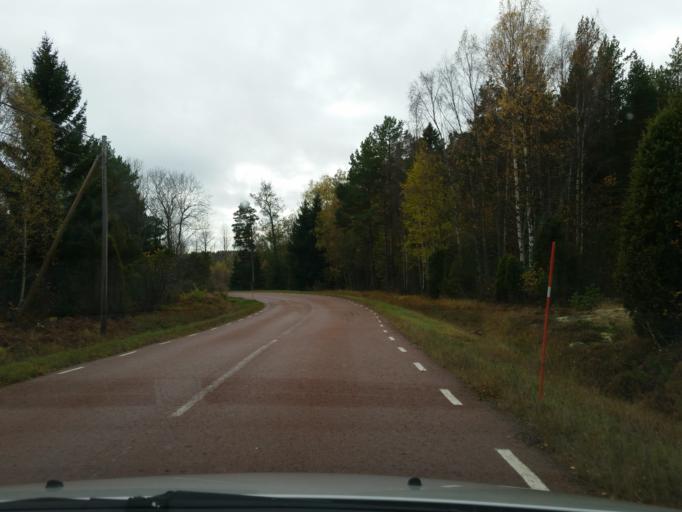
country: AX
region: Alands landsbygd
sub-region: Lemland
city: Lemland
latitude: 60.0307
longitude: 20.1704
